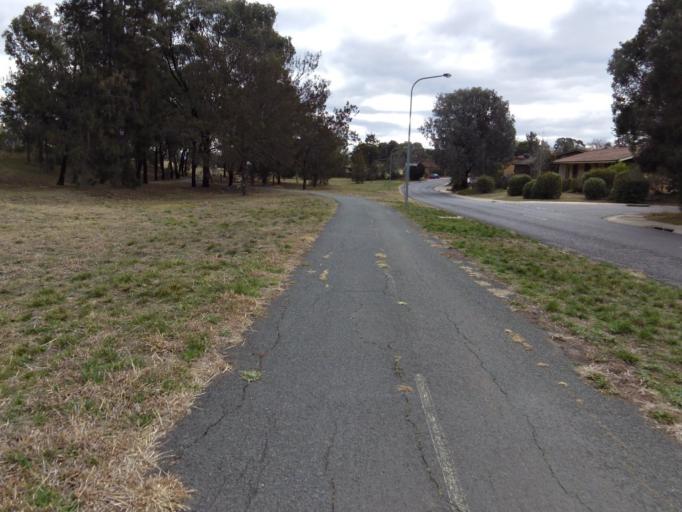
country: AU
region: Australian Capital Territory
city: Kaleen
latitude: -35.2354
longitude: 149.0976
